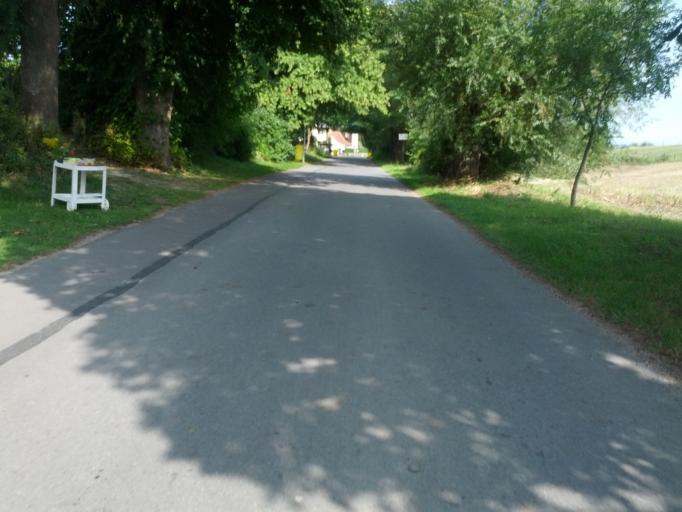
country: DE
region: Mecklenburg-Vorpommern
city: Bastorf
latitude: 54.1345
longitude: 11.6808
